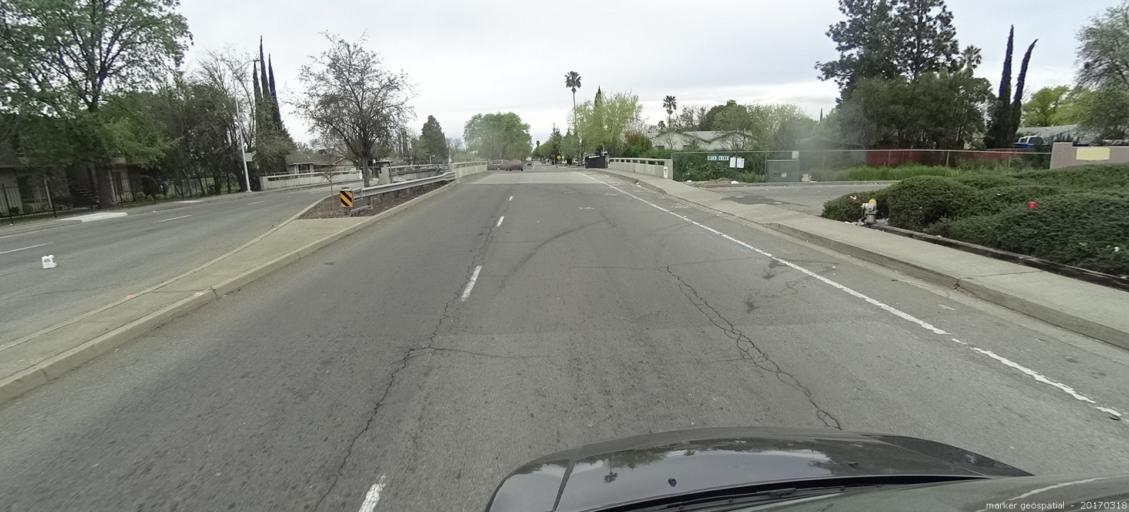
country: US
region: California
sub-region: Sacramento County
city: Parkway
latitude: 38.4752
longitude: -121.4373
